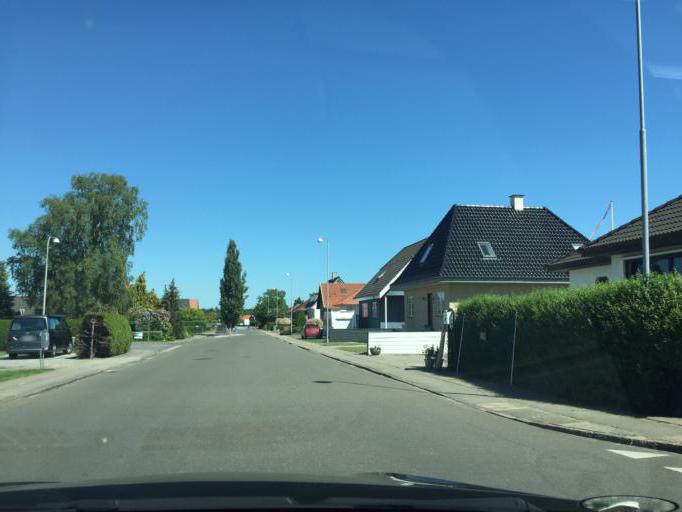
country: DK
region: South Denmark
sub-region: Odense Kommune
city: Odense
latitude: 55.3768
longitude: 10.3572
